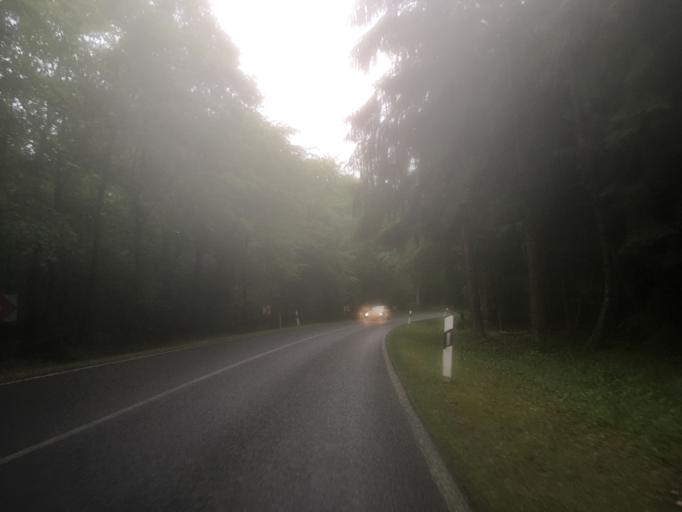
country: DE
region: Brandenburg
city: Zehdenick
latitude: 53.0459
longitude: 13.3151
